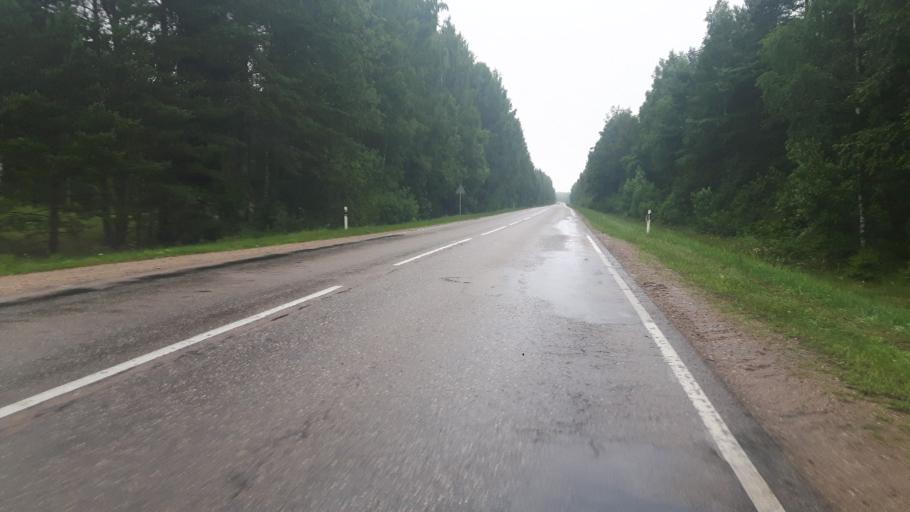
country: LV
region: Rucavas
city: Rucava
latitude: 56.1231
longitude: 21.1460
